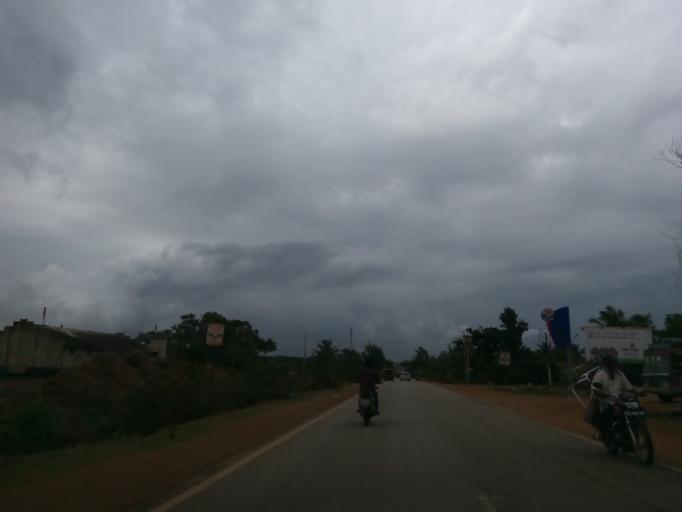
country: IN
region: Karnataka
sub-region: Davanagere
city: Harihar
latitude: 14.5323
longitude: 75.7702
